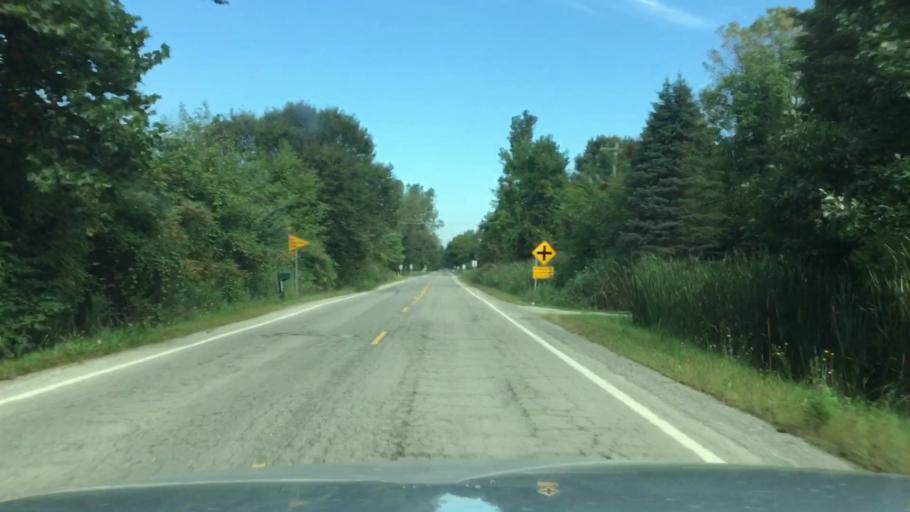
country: US
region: Michigan
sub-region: Wayne County
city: Belleville
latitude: 42.1584
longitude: -83.4613
